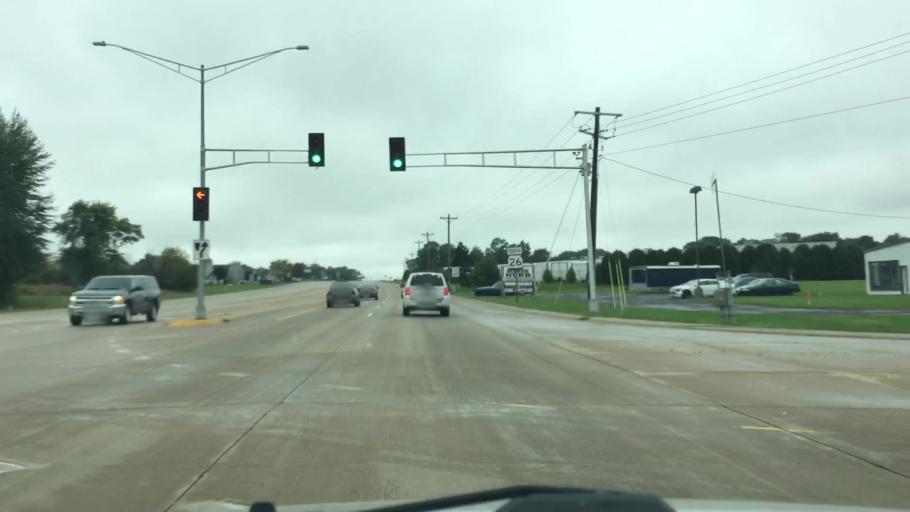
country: US
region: Wisconsin
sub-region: Rock County
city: Milton
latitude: 42.7388
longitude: -88.9780
